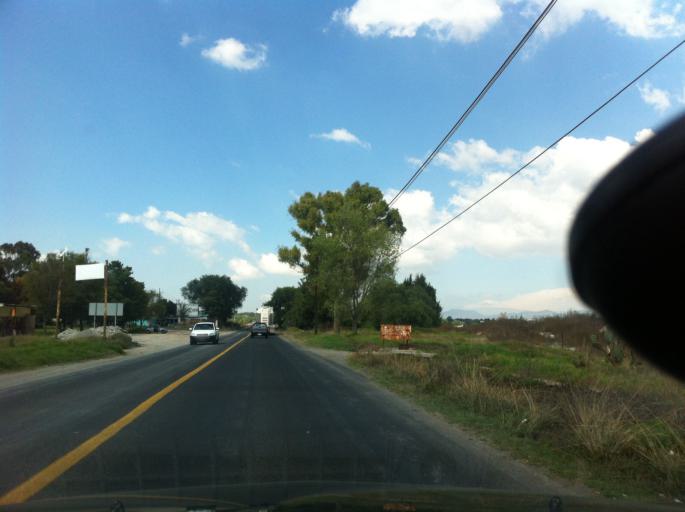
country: MX
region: Mexico
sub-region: Tequixquiac
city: Colonia Wenceslao Labra
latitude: 19.8291
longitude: -99.1180
